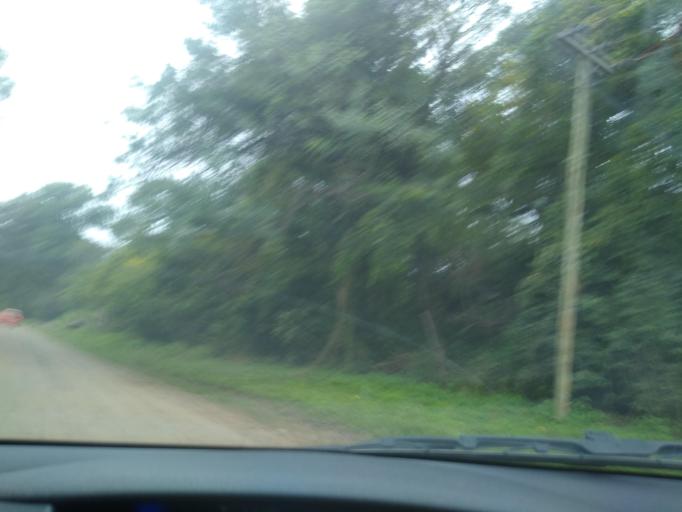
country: AR
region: Chaco
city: Colonia Benitez
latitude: -27.3359
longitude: -58.9573
